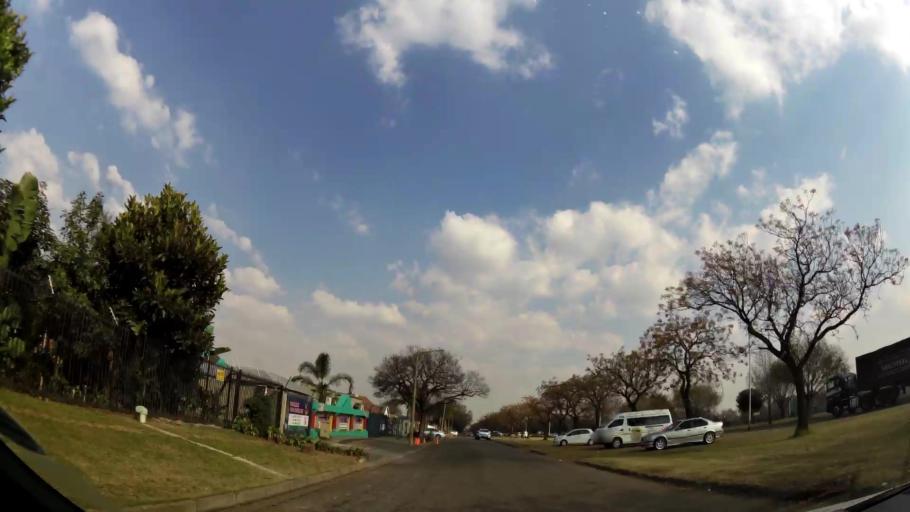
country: ZA
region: Gauteng
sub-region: Ekurhuleni Metropolitan Municipality
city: Boksburg
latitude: -26.2305
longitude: 28.2489
